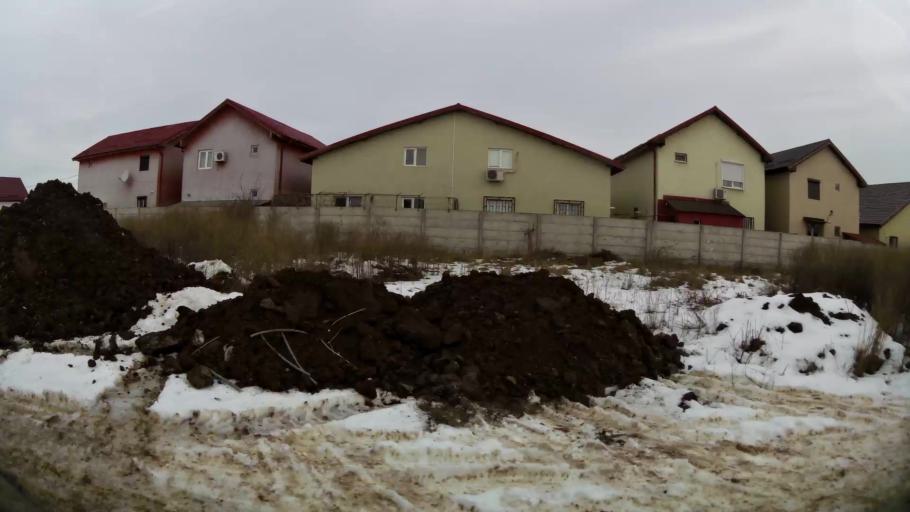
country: RO
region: Ilfov
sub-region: Comuna Pantelimon
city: Pantelimon
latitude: 44.4585
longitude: 26.1968
